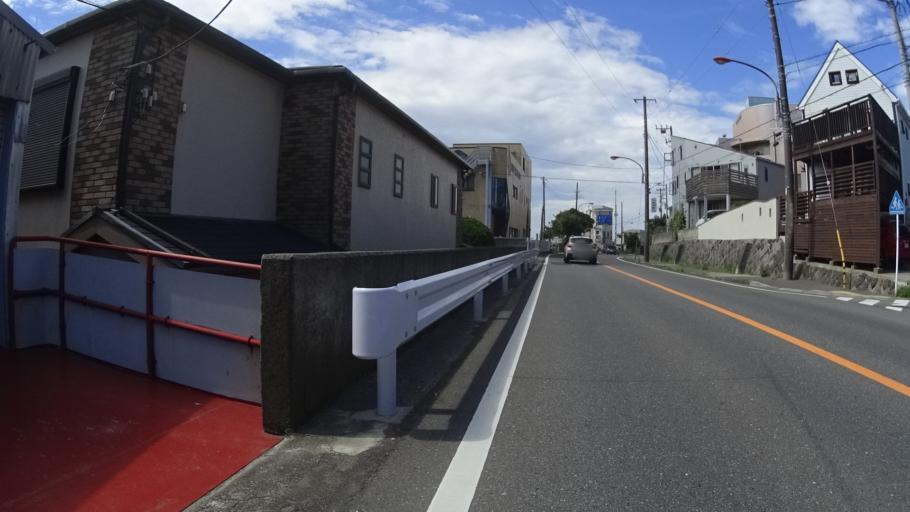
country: JP
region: Kanagawa
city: Yokosuka
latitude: 35.2070
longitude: 139.6835
